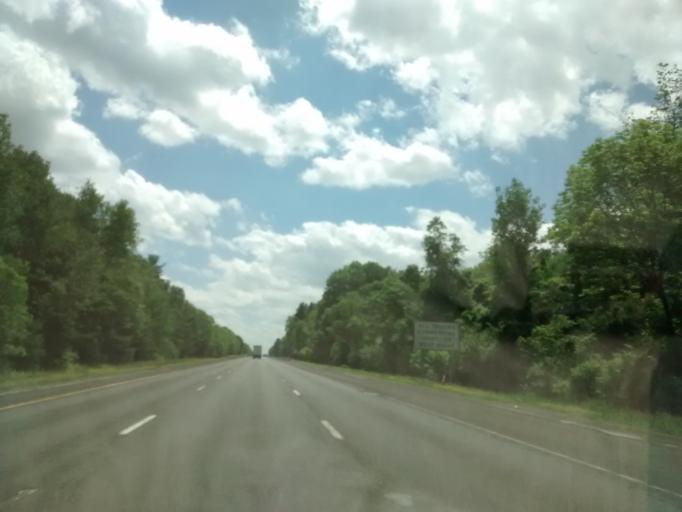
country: US
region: Massachusetts
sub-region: Hampden County
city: Holland
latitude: 42.0635
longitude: -72.1116
